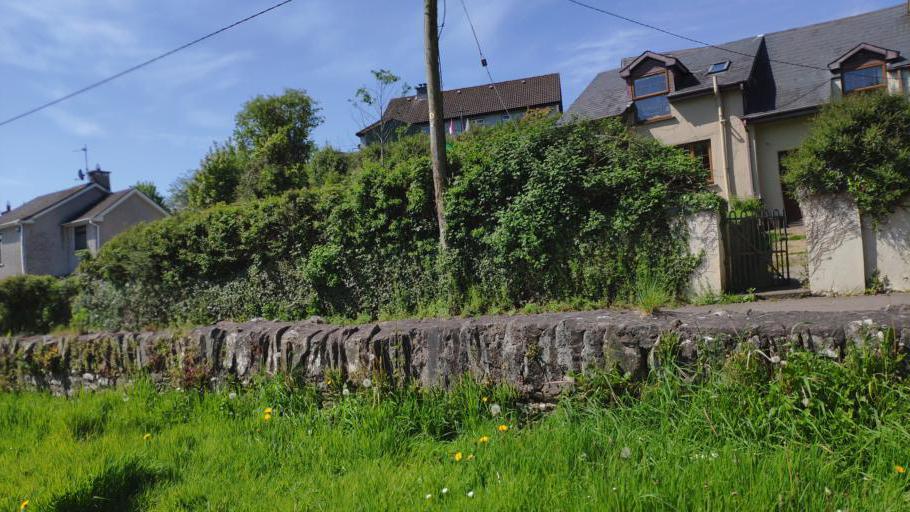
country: IE
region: Munster
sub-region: County Cork
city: Blarney
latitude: 51.9359
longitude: -8.5628
